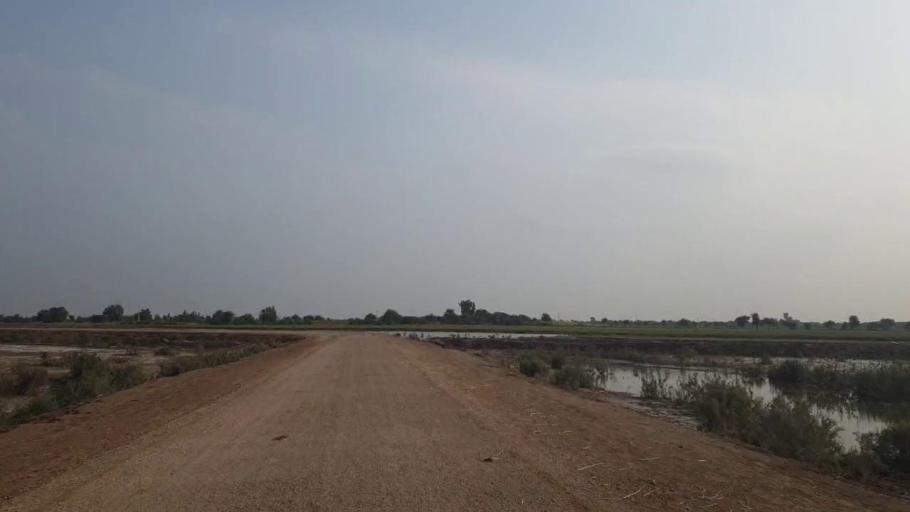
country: PK
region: Sindh
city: Badin
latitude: 24.6008
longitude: 68.6974
